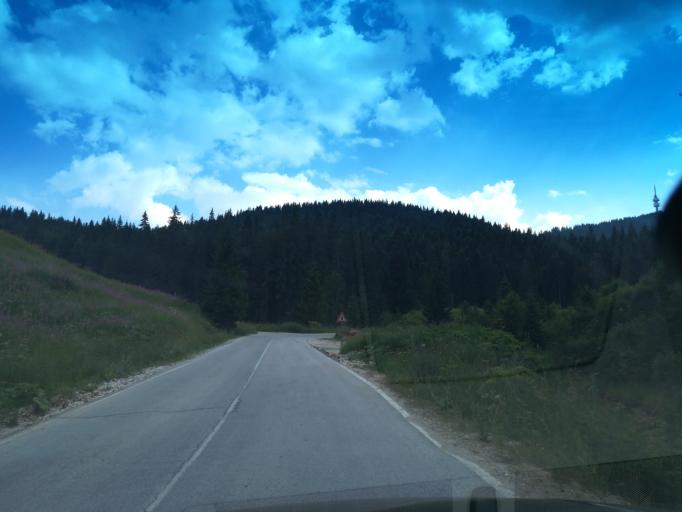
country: BG
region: Smolyan
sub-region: Obshtina Smolyan
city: Smolyan
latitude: 41.6544
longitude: 24.6880
